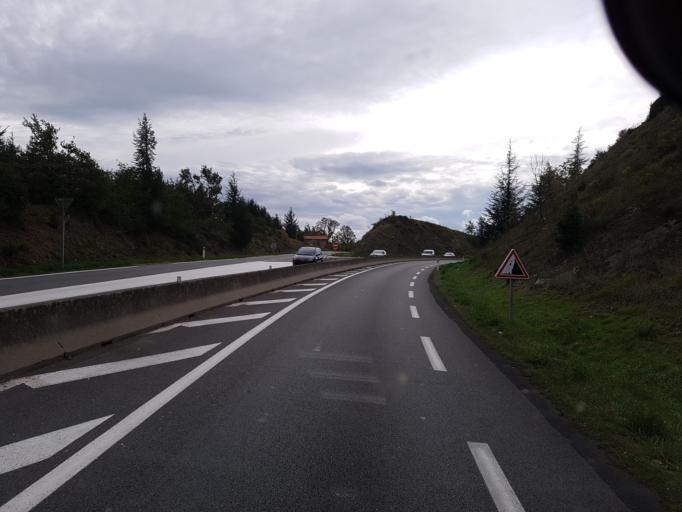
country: FR
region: Rhone-Alpes
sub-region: Departement de la Loire
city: Saint-Genest-Lerpt
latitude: 45.4432
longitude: 4.3421
